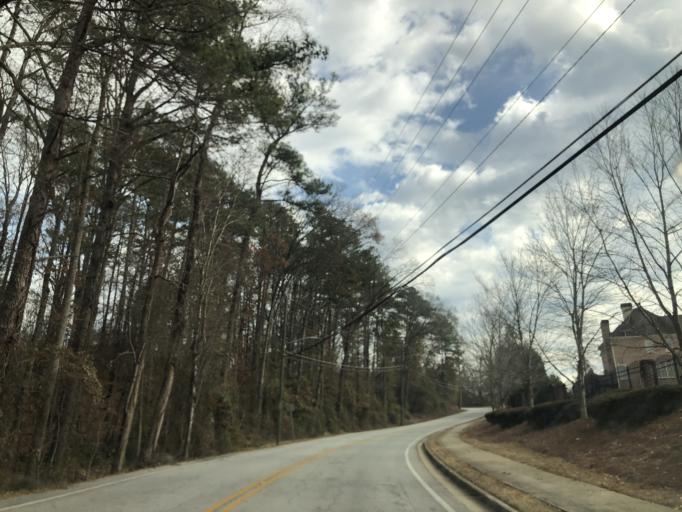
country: US
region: Georgia
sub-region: DeKalb County
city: Panthersville
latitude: 33.6652
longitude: -84.2056
